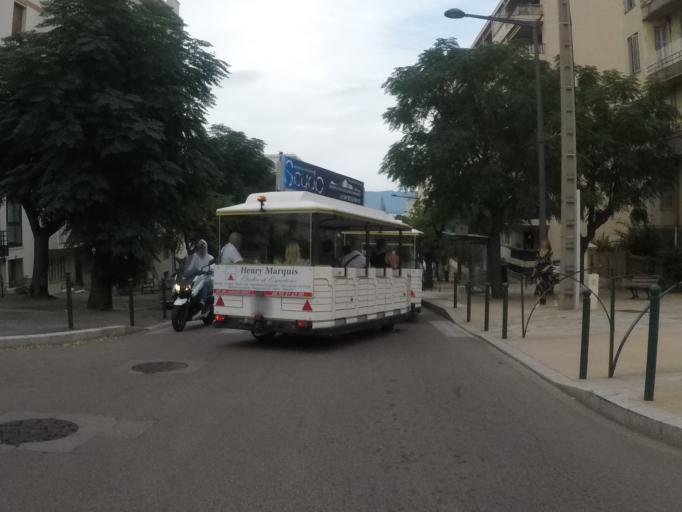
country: FR
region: Corsica
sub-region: Departement de la Corse-du-Sud
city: Ajaccio
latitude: 41.9145
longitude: 8.7248
